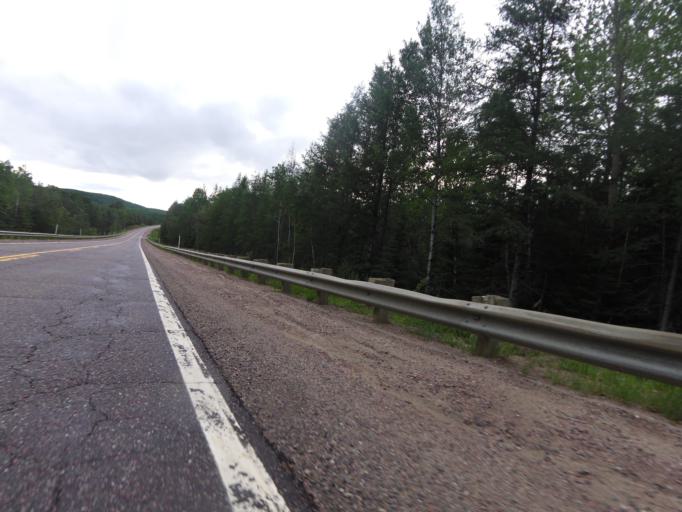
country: CA
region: Quebec
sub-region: Outaouais
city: Shawville
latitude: 45.9070
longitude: -76.2952
